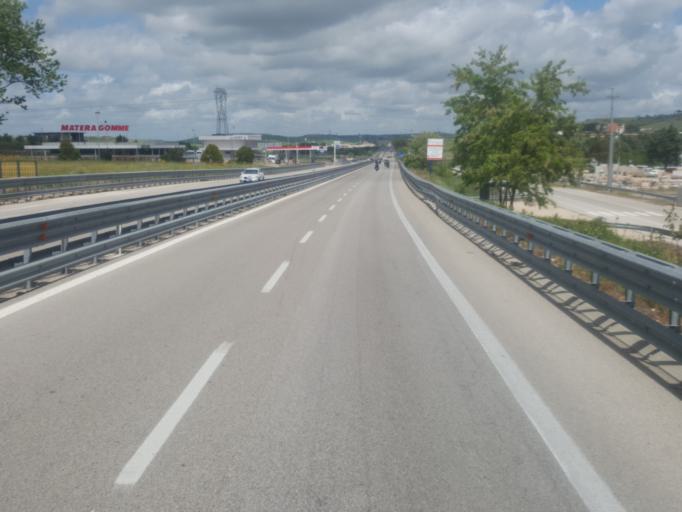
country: IT
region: Basilicate
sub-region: Provincia di Matera
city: Matera
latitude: 40.7087
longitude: 16.5815
